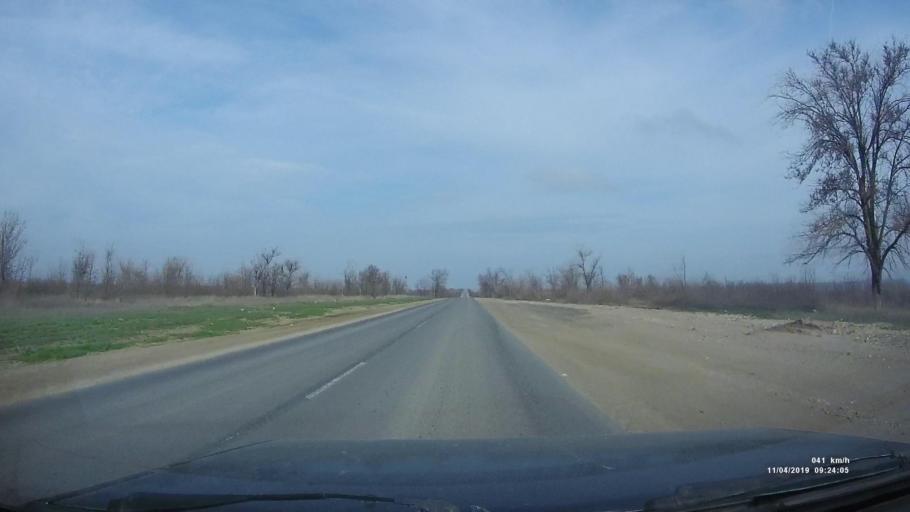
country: RU
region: Rostov
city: Staraya Stanitsa
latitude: 48.2473
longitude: 40.3855
